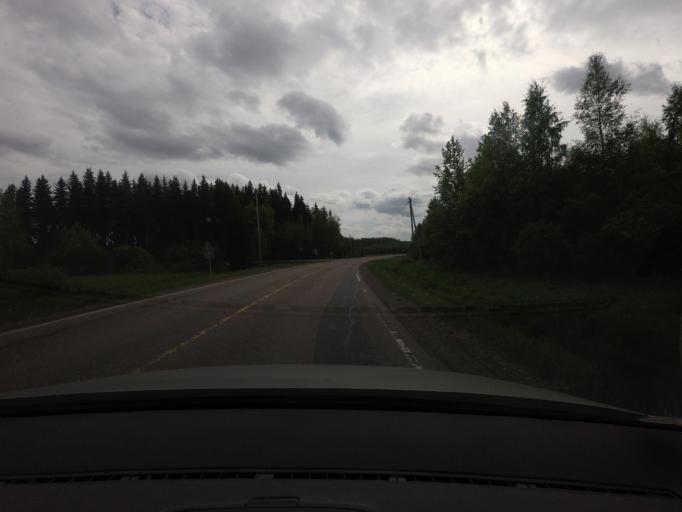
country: FI
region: South Karelia
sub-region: Lappeenranta
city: Taavetti
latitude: 60.9108
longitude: 27.5724
